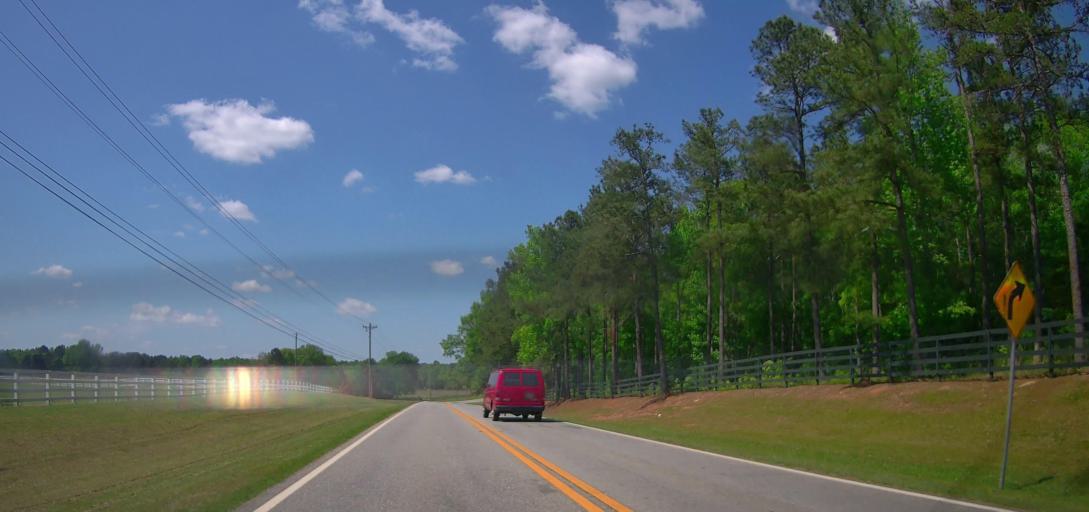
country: US
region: Georgia
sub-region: Putnam County
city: Eatonton
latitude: 33.2963
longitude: -83.3027
